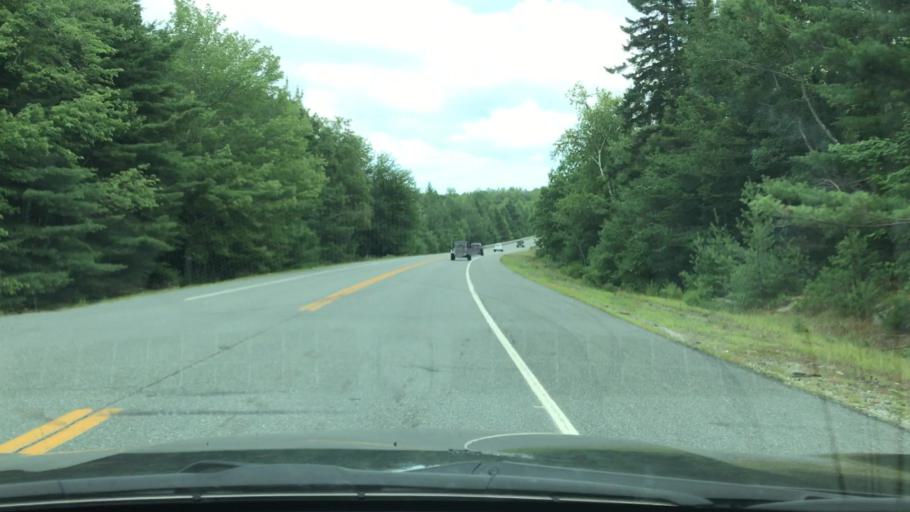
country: US
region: Maine
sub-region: Hancock County
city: Surry
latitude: 44.5569
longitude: -68.5460
